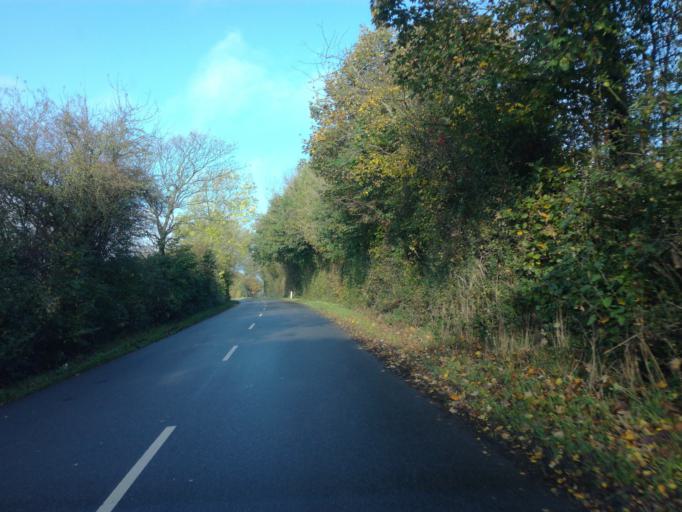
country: DK
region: South Denmark
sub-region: Vejle Kommune
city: Borkop
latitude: 55.6497
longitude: 9.6598
